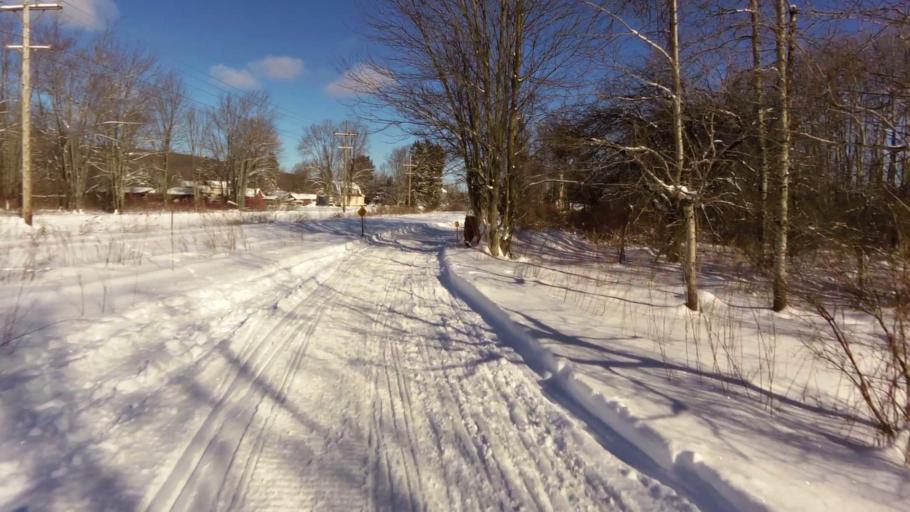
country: US
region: New York
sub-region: Cattaraugus County
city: Randolph
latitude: 42.2967
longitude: -79.0915
